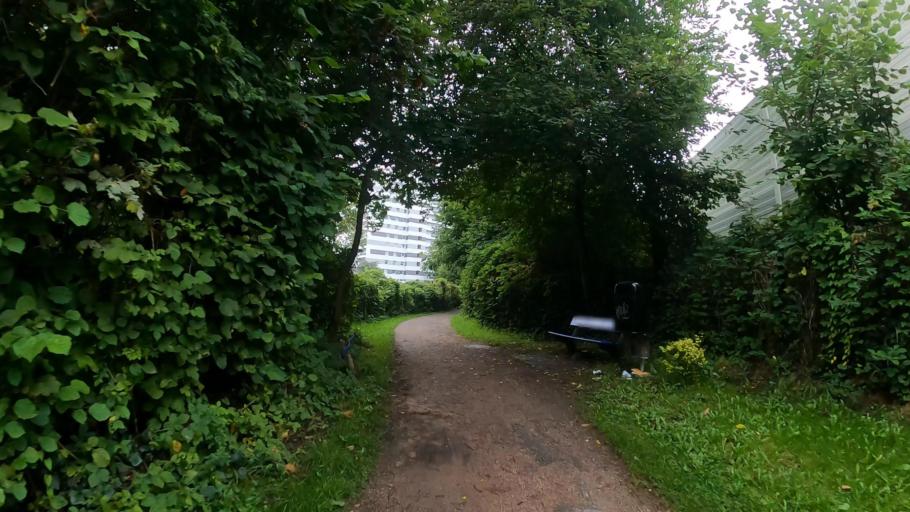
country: DE
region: Schleswig-Holstein
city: Rellingen
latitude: 53.6505
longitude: 9.8042
